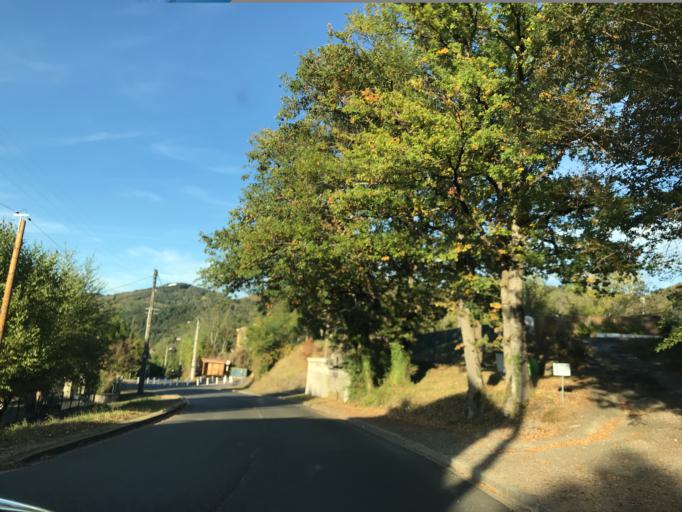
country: FR
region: Auvergne
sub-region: Departement du Puy-de-Dome
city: Thiers
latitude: 45.8731
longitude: 3.5304
